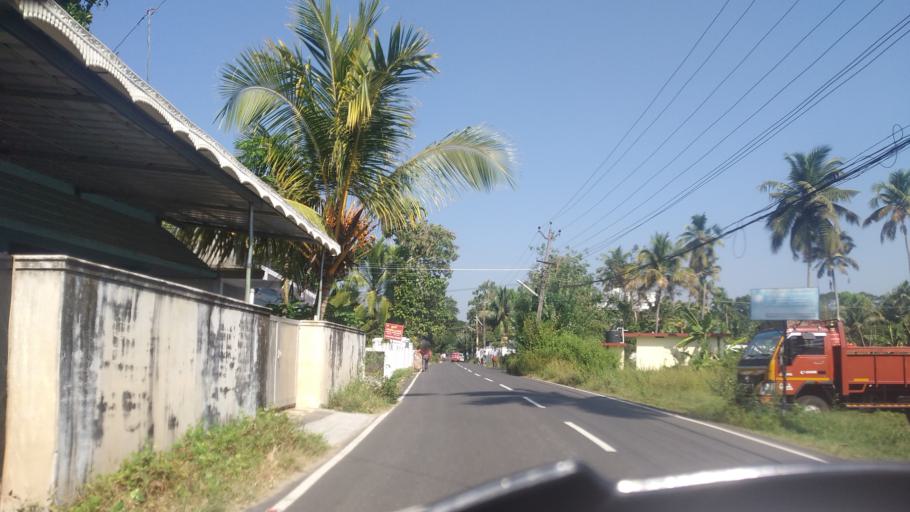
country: IN
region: Kerala
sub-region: Ernakulam
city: Elur
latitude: 10.1163
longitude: 76.2475
